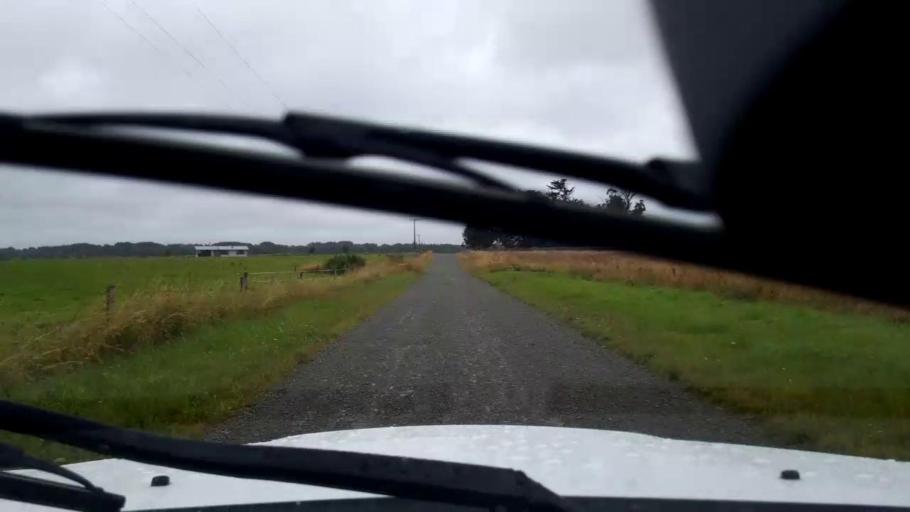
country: NZ
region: Canterbury
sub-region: Timaru District
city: Pleasant Point
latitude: -44.2489
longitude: 171.2006
